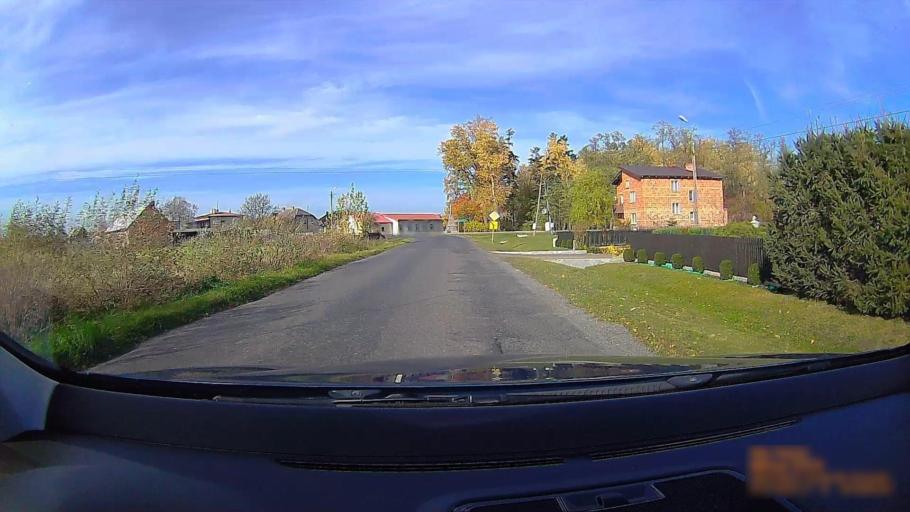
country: PL
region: Greater Poland Voivodeship
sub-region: Powiat ostrzeszowski
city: Doruchow
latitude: 51.4270
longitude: 18.0518
